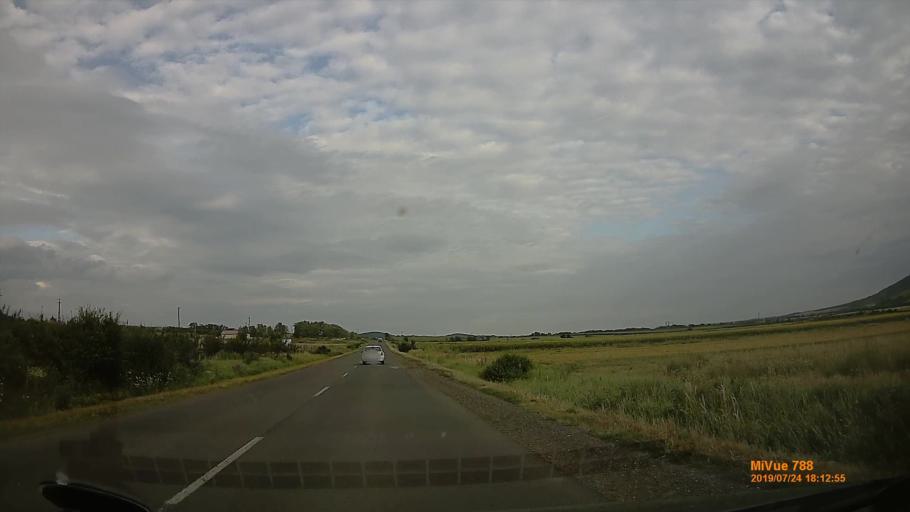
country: HU
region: Borsod-Abauj-Zemplen
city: Tallya
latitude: 48.2331
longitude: 21.2142
